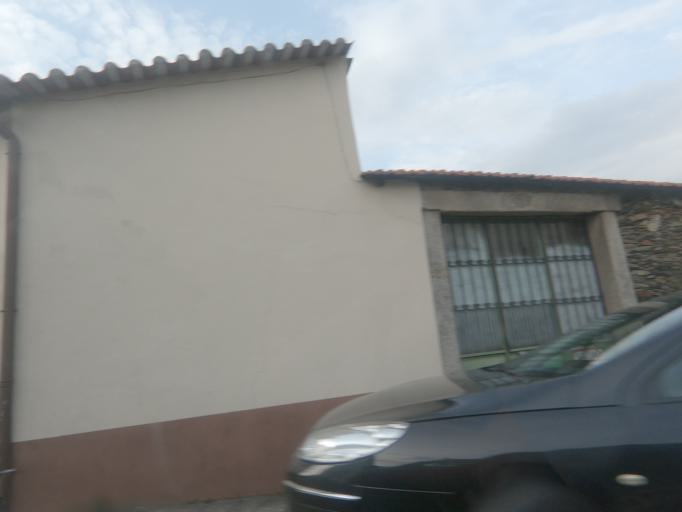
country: PT
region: Porto
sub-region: Valongo
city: Valongo
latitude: 41.1899
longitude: -8.5046
